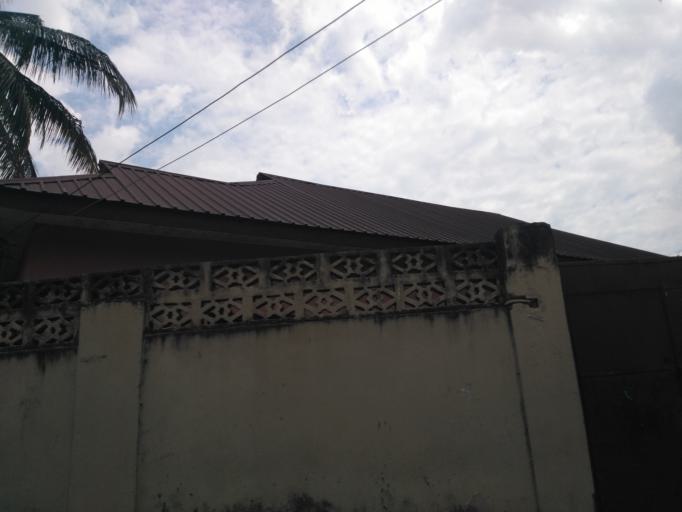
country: TZ
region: Dar es Salaam
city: Magomeni
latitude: -6.7567
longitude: 39.2411
